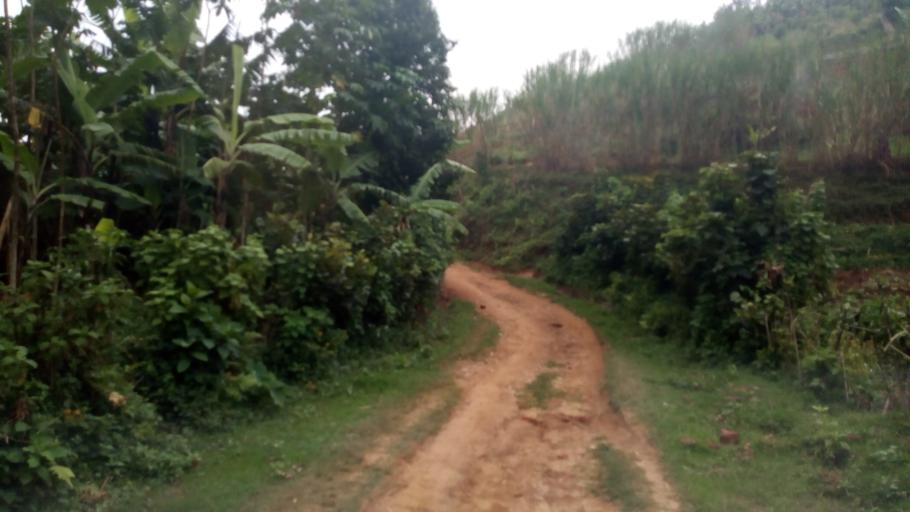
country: UG
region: Western Region
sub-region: Kisoro District
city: Kisoro
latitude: -1.2430
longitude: 29.6176
